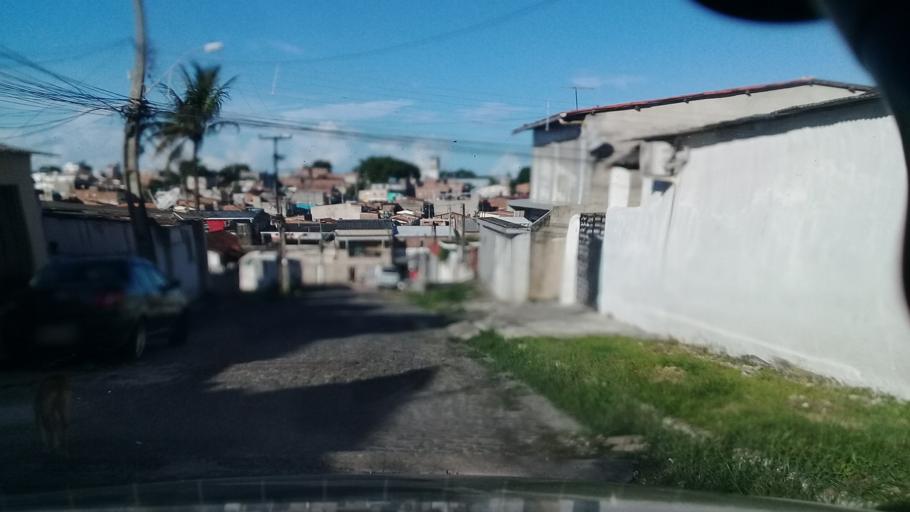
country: BR
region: Pernambuco
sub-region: Jaboatao Dos Guararapes
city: Jaboatao dos Guararapes
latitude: -8.1161
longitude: -34.9542
